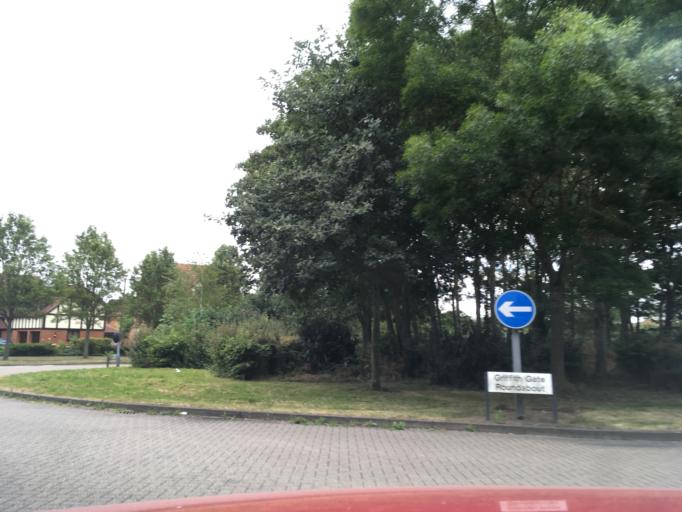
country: GB
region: England
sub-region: Milton Keynes
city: Broughton
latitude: 52.0428
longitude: -0.6993
